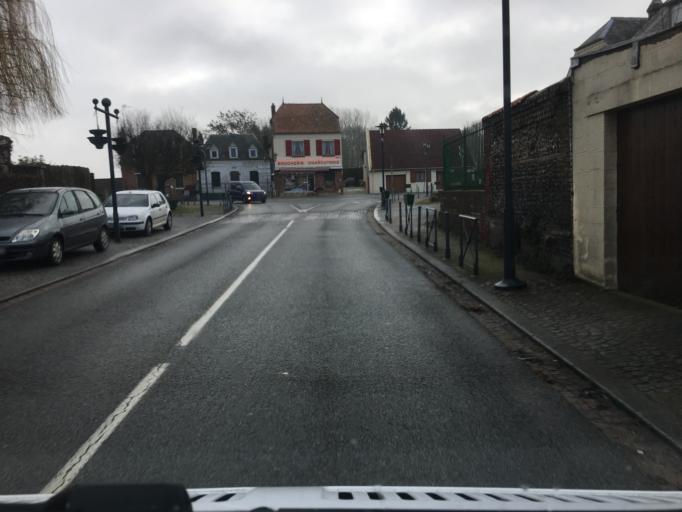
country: FR
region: Picardie
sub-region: Departement de la Somme
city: Sailly-Flibeaucourt
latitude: 50.1846
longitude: 1.7087
